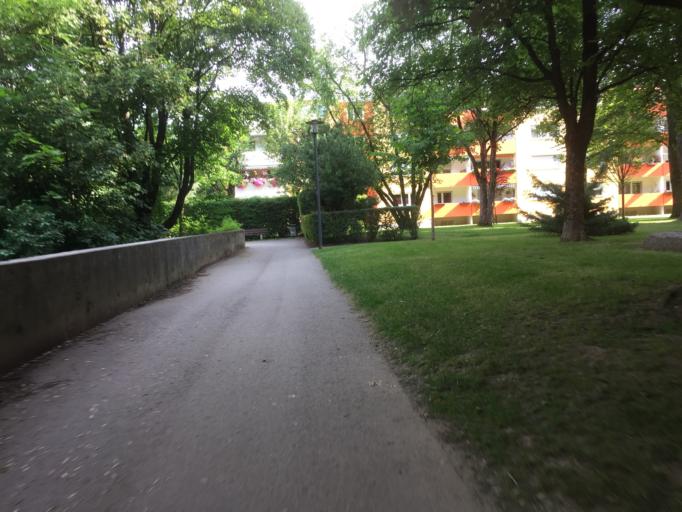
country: DE
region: Bavaria
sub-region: Upper Bavaria
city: Neubiberg
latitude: 48.1088
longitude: 11.6341
